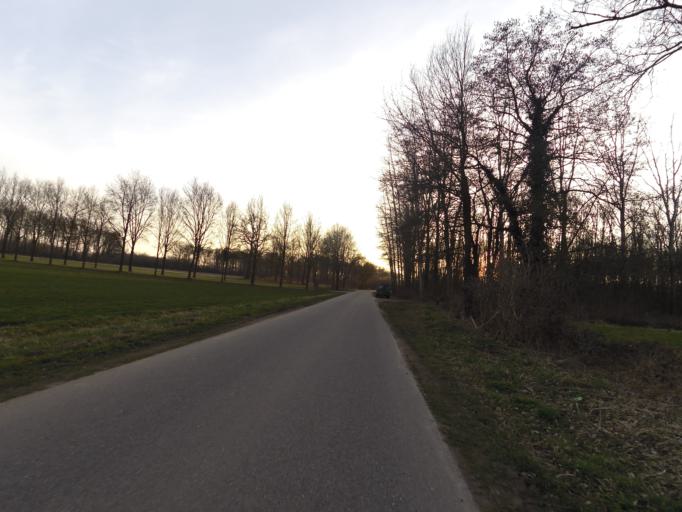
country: NL
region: Gelderland
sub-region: Gemeente Zevenaar
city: Zevenaar
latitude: 51.9469
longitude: 6.1099
